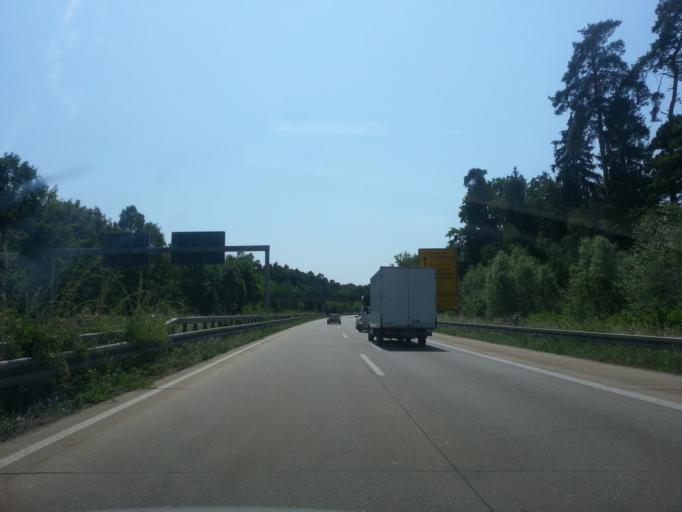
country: DE
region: Hesse
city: Dieburg
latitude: 49.8993
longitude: 8.8670
